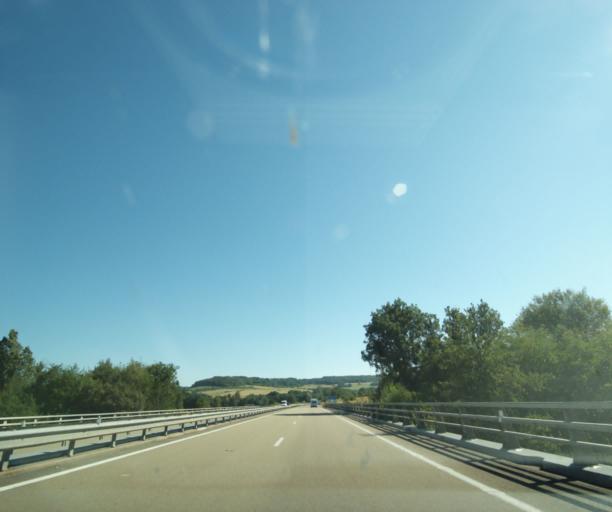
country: FR
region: Champagne-Ardenne
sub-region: Departement de la Haute-Marne
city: Rolampont
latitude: 47.9368
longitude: 5.2936
